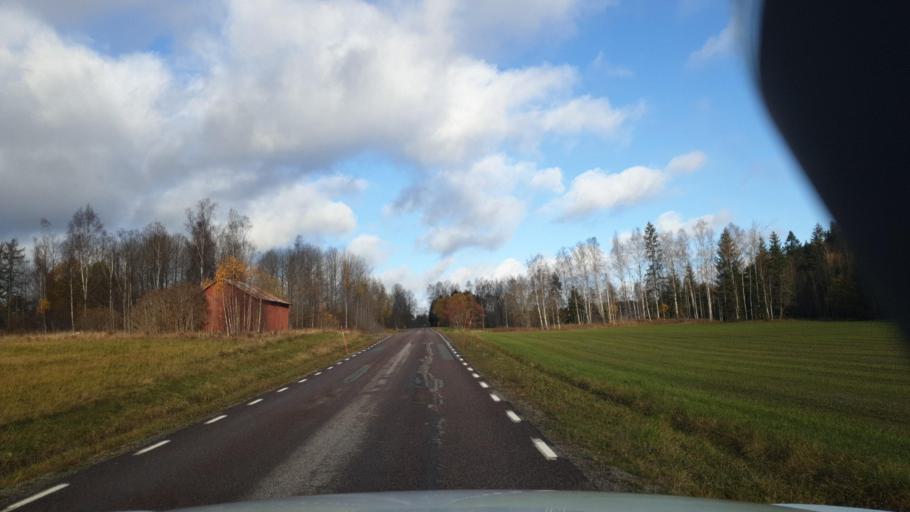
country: SE
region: Vaermland
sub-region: Grums Kommun
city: Slottsbron
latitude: 59.4615
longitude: 12.8768
